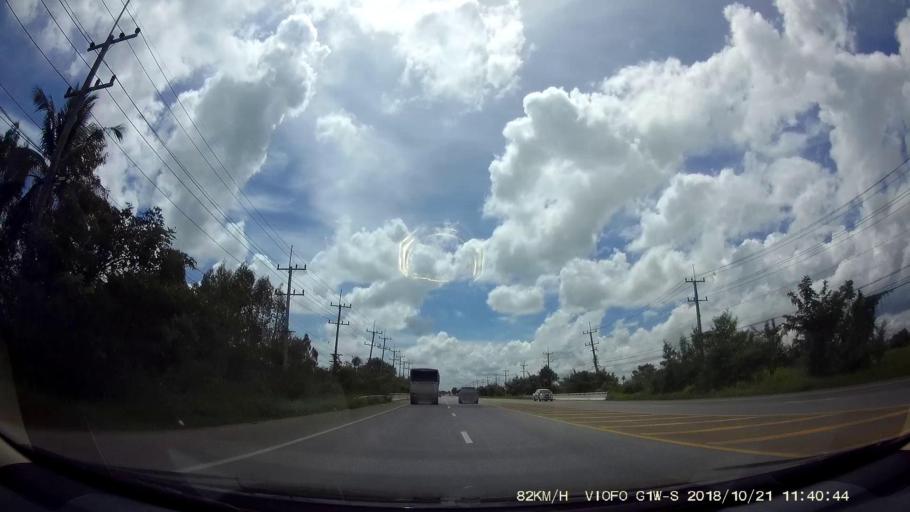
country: TH
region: Chaiyaphum
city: Chaiyaphum
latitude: 15.7094
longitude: 102.0154
